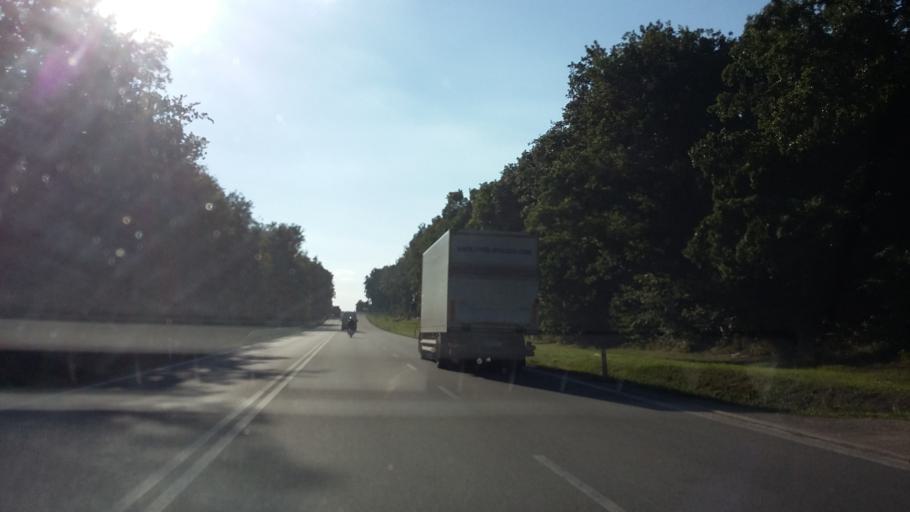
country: CZ
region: South Moravian
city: Troubsko
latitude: 49.1896
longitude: 16.4618
